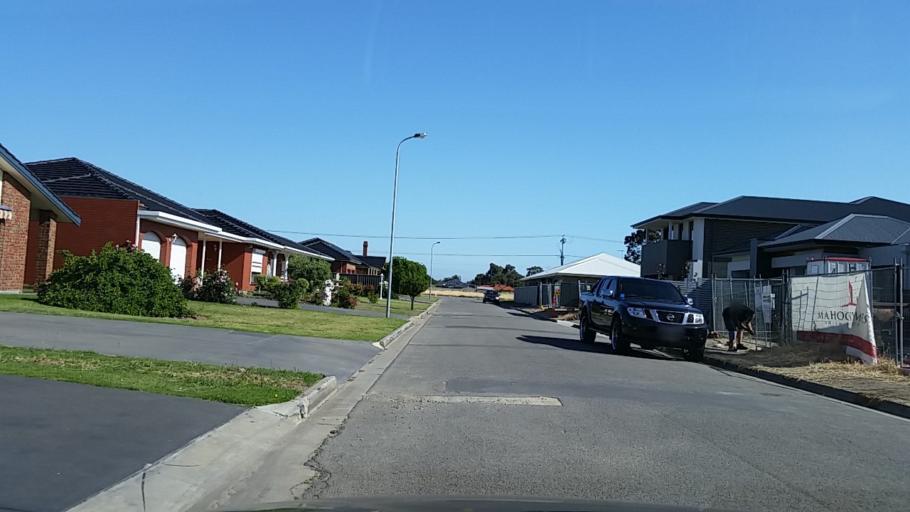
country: AU
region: South Australia
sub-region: Charles Sturt
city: Henley Beach
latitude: -34.9193
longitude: 138.5072
